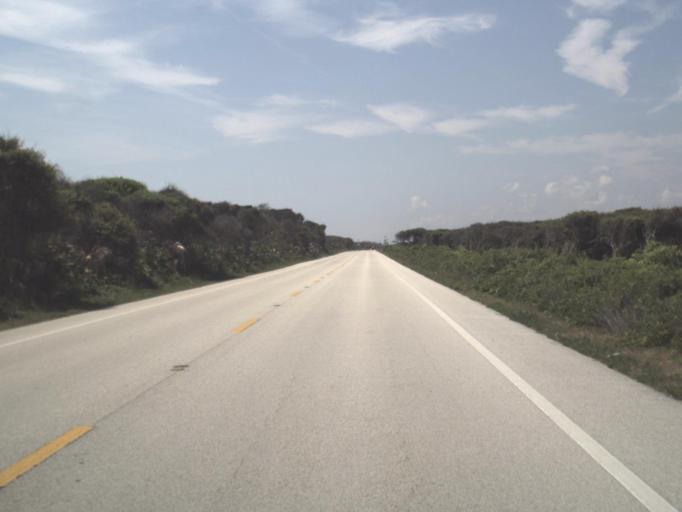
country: US
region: Florida
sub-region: Saint Johns County
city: Palm Valley
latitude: 30.0785
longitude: -81.3362
